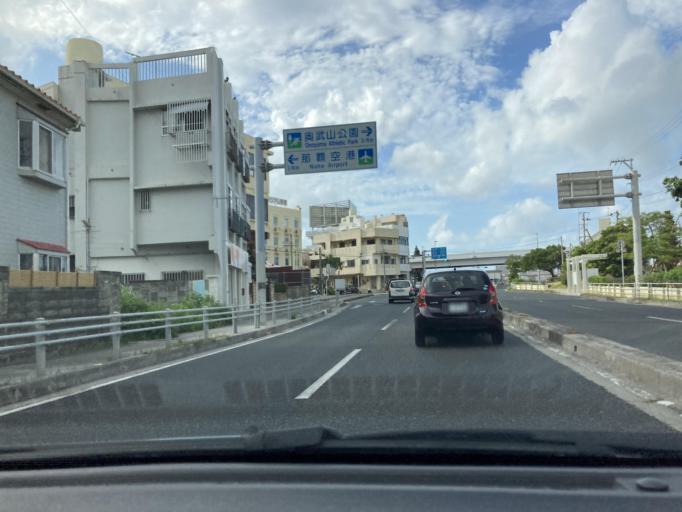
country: JP
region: Okinawa
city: Naha-shi
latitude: 26.2033
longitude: 127.6718
